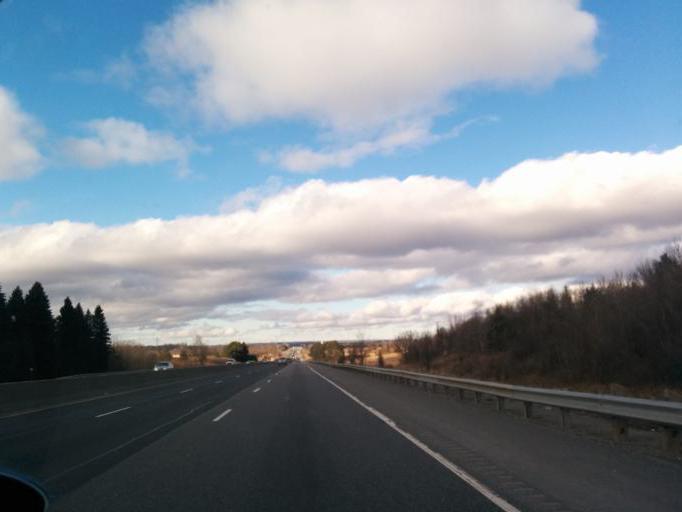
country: CA
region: Ontario
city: Newmarket
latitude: 43.9667
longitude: -79.5770
